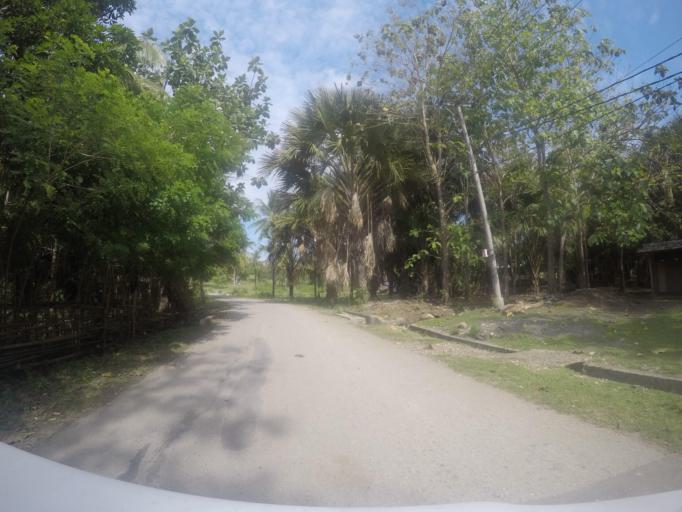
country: TL
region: Viqueque
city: Viqueque
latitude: -8.8533
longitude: 126.3586
